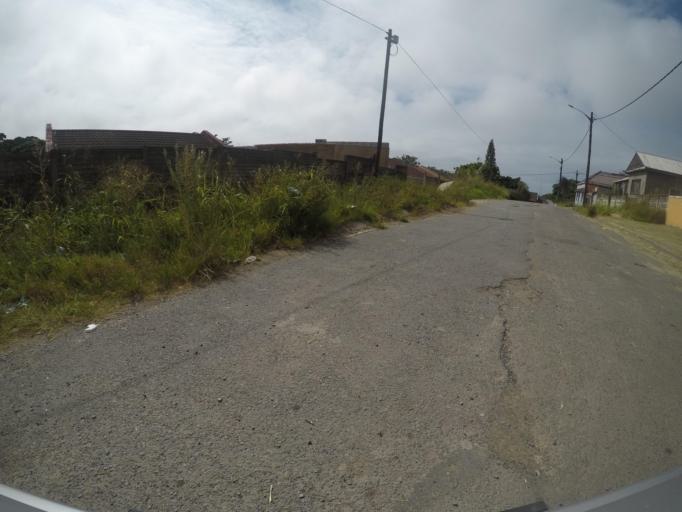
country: ZA
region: Eastern Cape
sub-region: Buffalo City Metropolitan Municipality
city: East London
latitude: -32.9990
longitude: 27.9114
